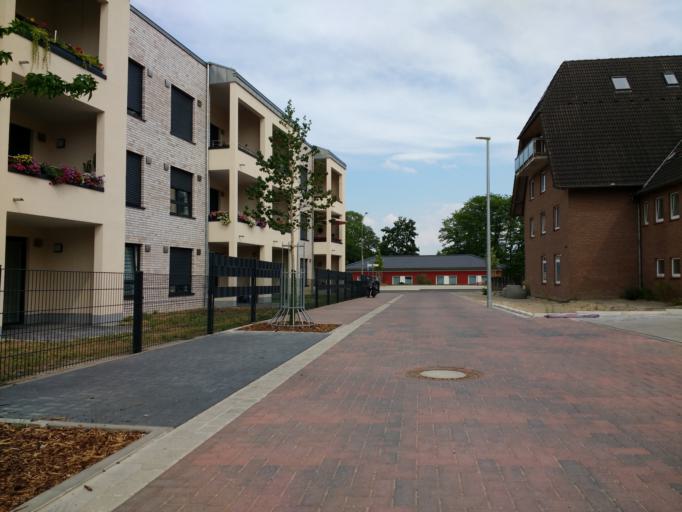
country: DE
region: Lower Saxony
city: Gifhorn
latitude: 52.4960
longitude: 10.5407
